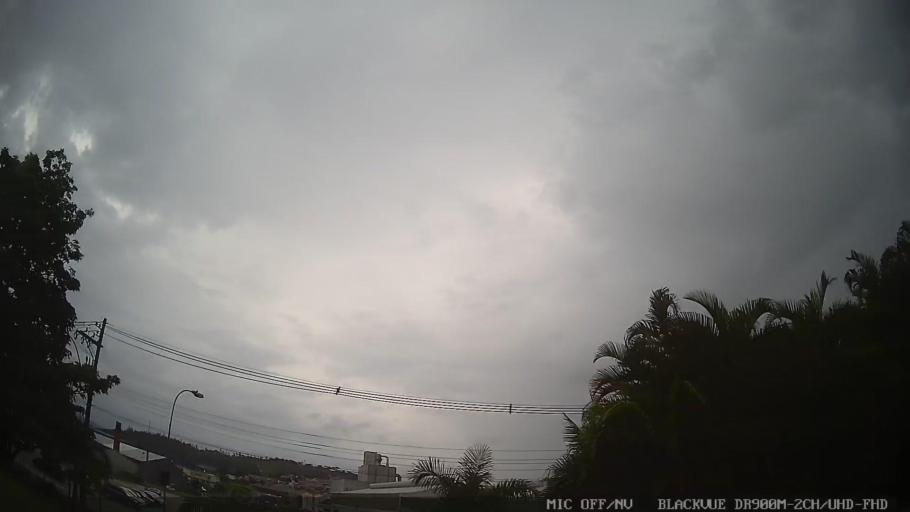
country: BR
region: Sao Paulo
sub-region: Amparo
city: Amparo
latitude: -22.7205
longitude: -46.7877
